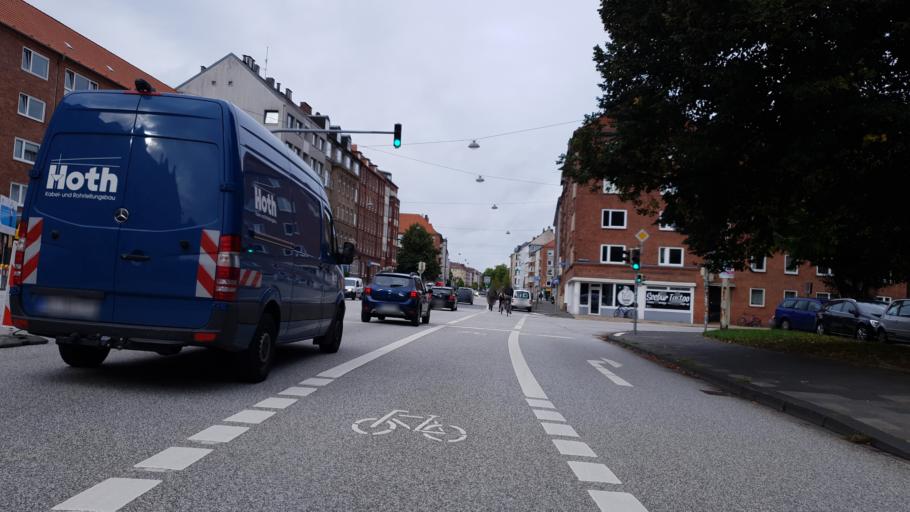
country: DE
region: Schleswig-Holstein
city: Kiel
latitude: 54.3355
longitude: 10.1302
